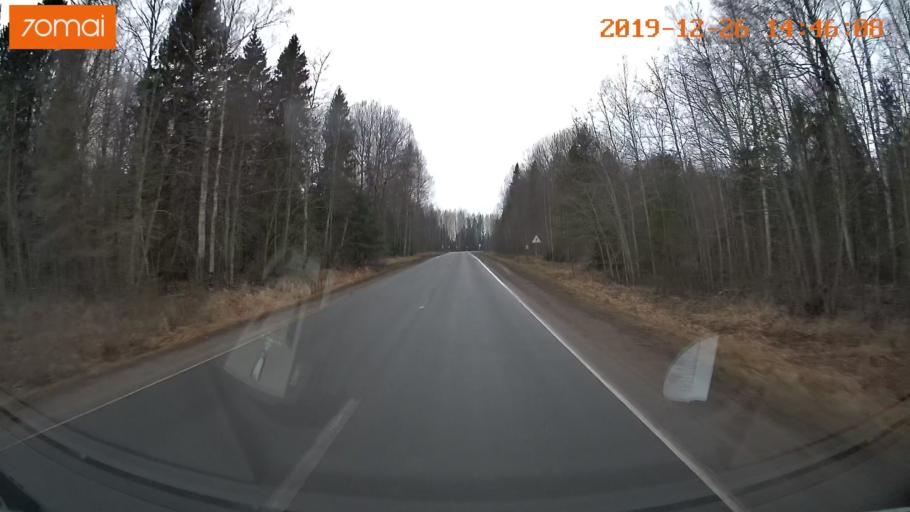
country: RU
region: Jaroslavl
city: Poshekhon'ye
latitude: 58.3347
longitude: 39.0236
